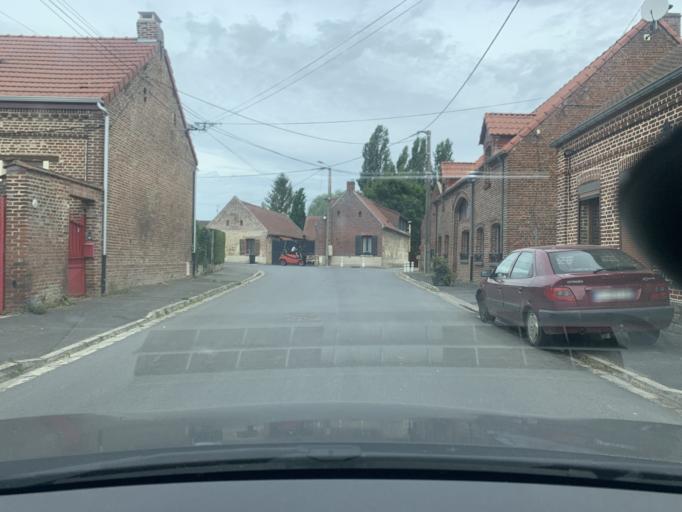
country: FR
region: Nord-Pas-de-Calais
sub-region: Departement du Nord
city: Marcoing
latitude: 50.1406
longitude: 3.1793
